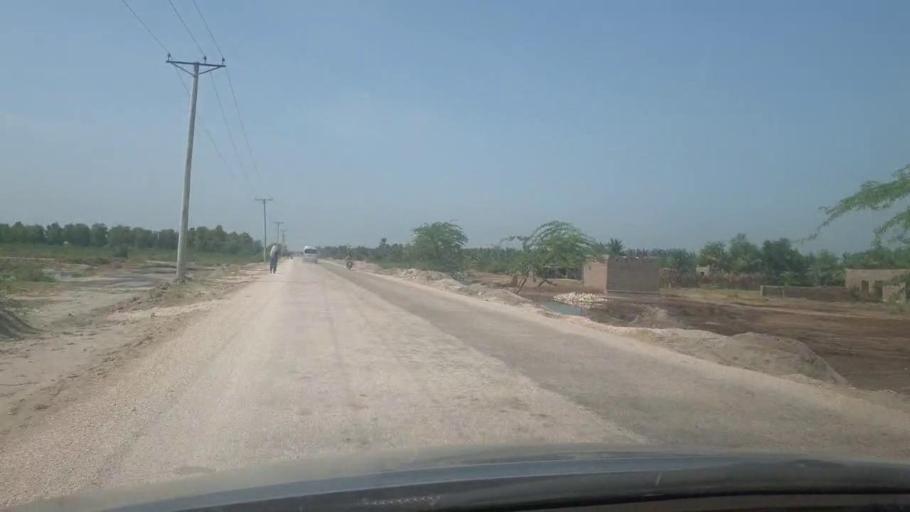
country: PK
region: Sindh
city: Ranipur
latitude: 27.2713
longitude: 68.5955
